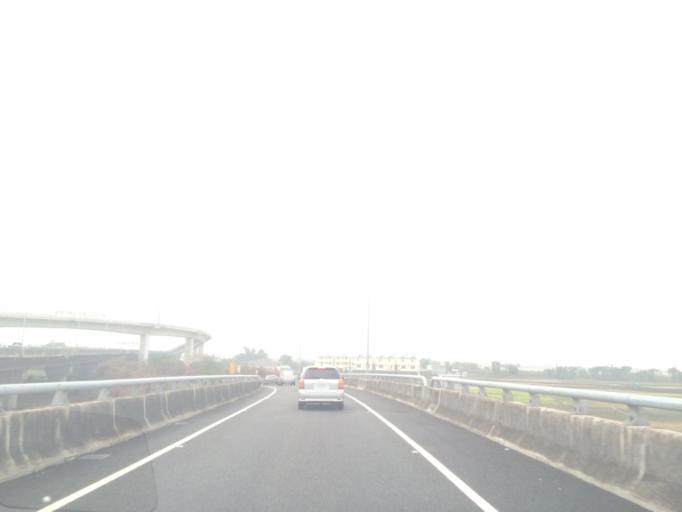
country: TW
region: Taiwan
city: Zhongxing New Village
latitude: 24.0292
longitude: 120.6697
